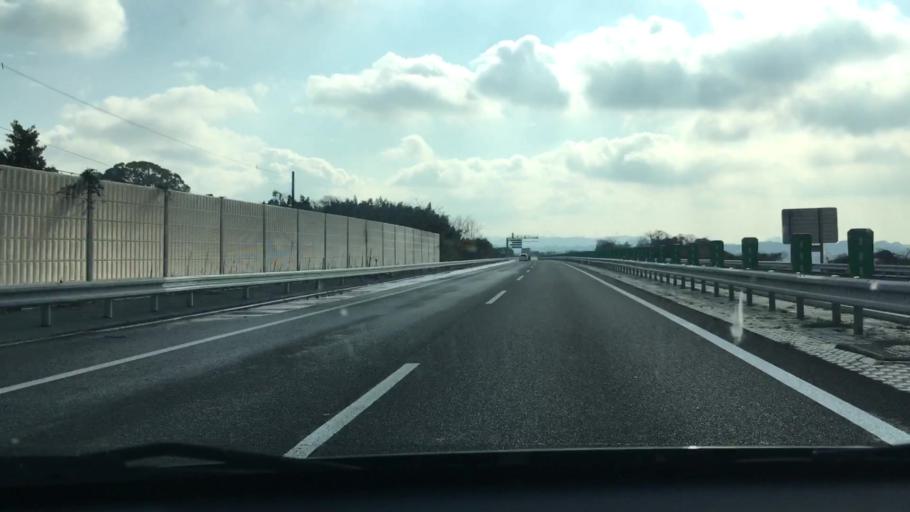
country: JP
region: Kumamoto
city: Uto
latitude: 32.7233
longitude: 130.7713
